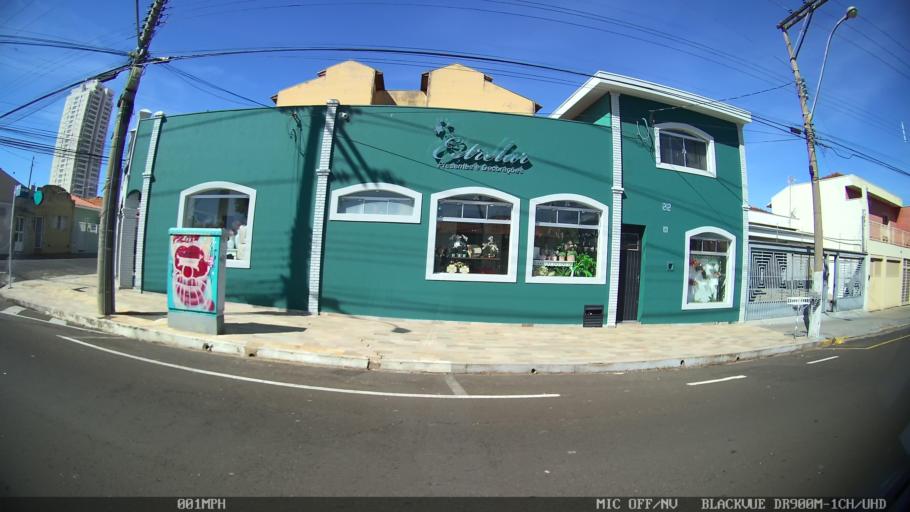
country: BR
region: Sao Paulo
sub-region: Franca
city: Franca
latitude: -20.5296
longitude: -47.3987
